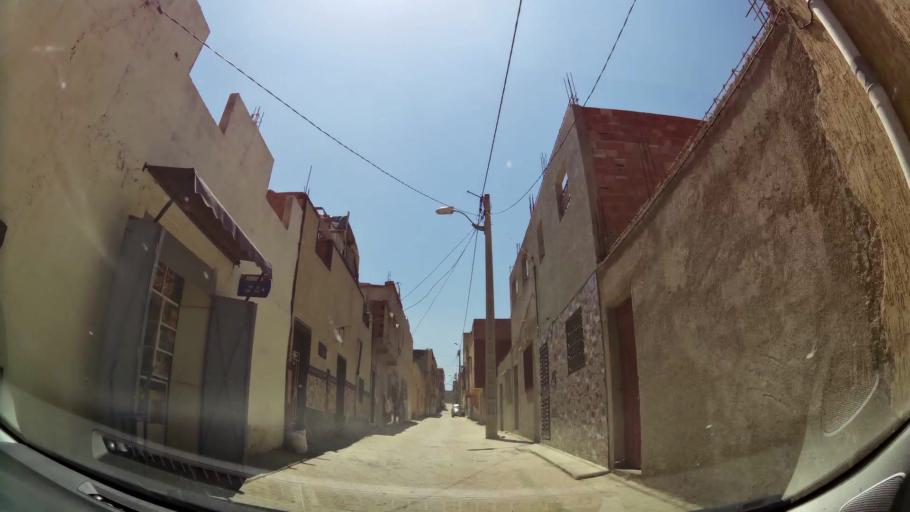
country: MA
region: Oriental
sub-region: Oujda-Angad
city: Oujda
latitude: 34.6795
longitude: -1.9550
